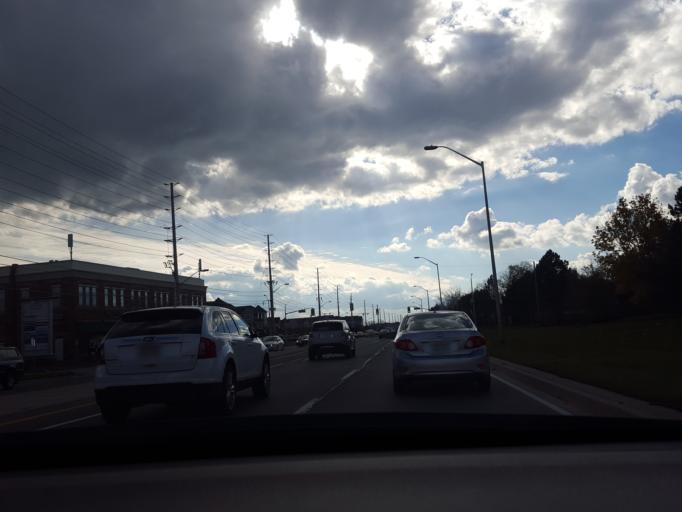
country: CA
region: Ontario
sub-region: Halton
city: Milton
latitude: 43.5125
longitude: -79.8551
